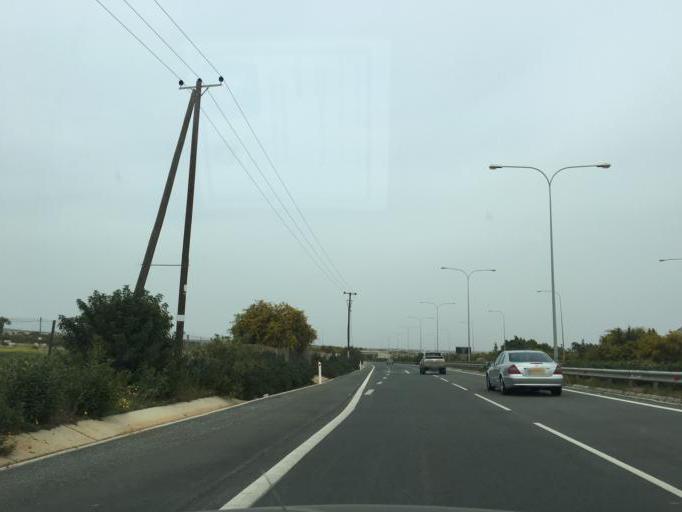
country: CY
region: Ammochostos
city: Ayia Napa
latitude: 34.9914
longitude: 33.9559
